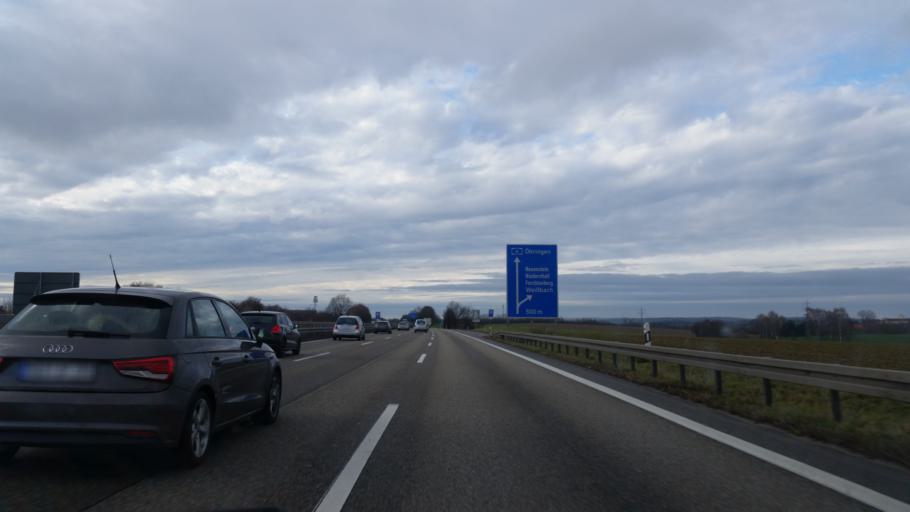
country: DE
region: Baden-Wuerttemberg
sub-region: Regierungsbezirk Stuttgart
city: Neuenstein
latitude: 49.2148
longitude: 9.6030
